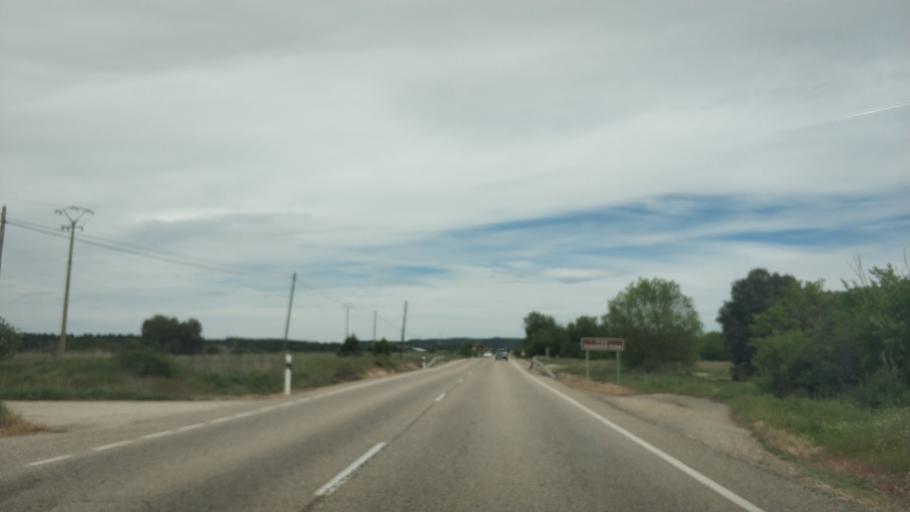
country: ES
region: Castille and Leon
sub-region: Provincia de Soria
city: Bayubas de Abajo
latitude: 41.4983
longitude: -2.8786
